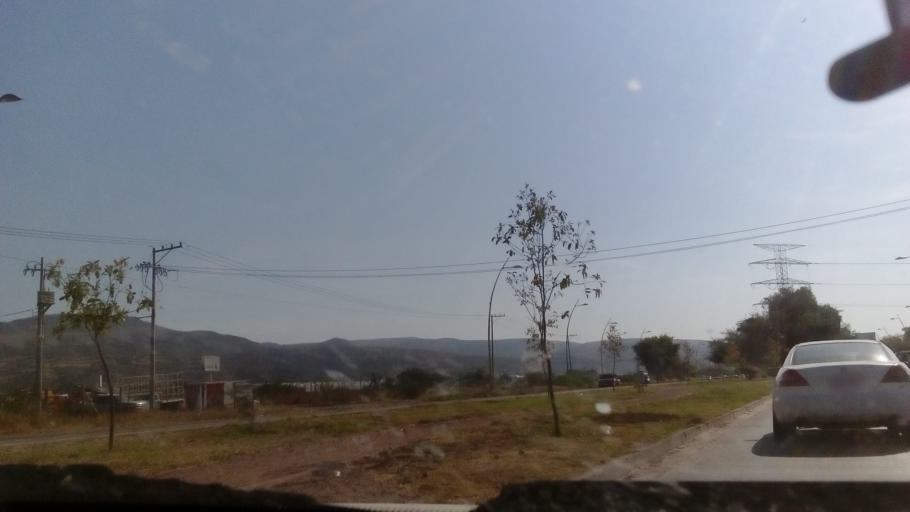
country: MX
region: Guanajuato
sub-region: Leon
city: Medina
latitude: 21.1387
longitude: -101.6239
